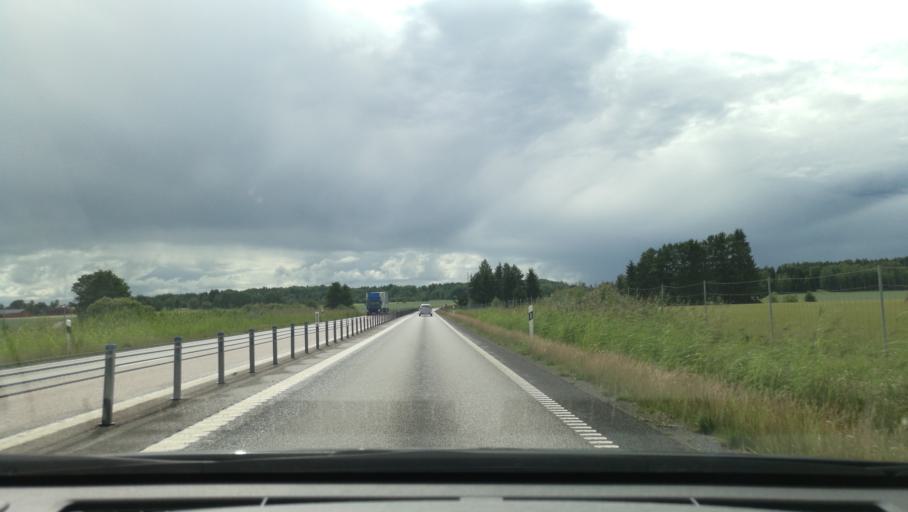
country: SE
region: Vaestmanland
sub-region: Kopings Kommun
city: Koping
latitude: 59.5575
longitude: 16.0525
